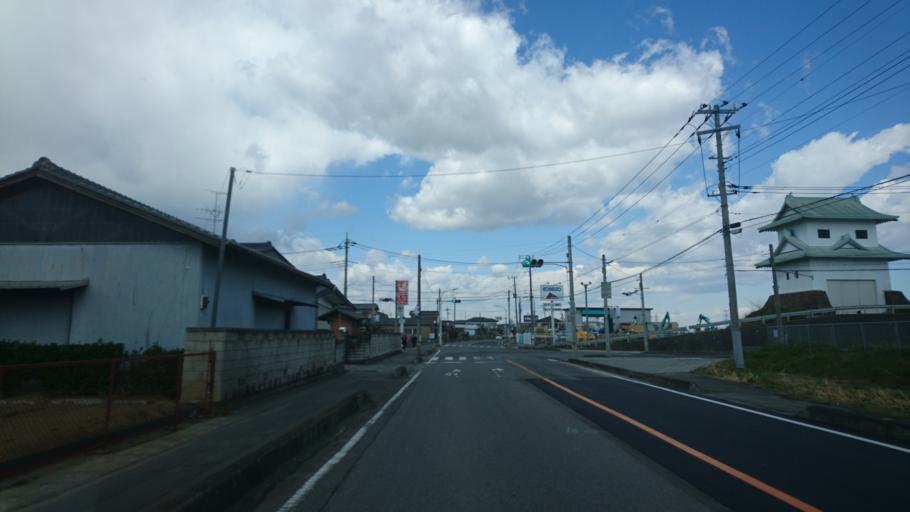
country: JP
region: Ibaraki
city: Ishige
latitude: 36.1138
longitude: 139.9790
